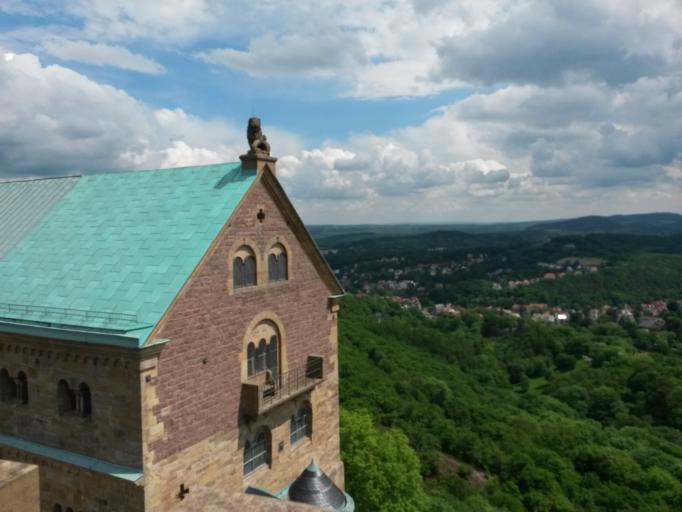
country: DE
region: Thuringia
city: Eisenach
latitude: 50.9655
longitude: 10.3062
